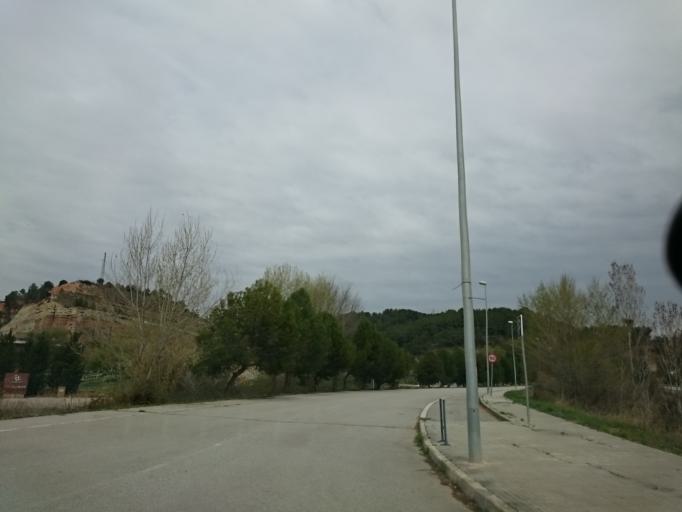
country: ES
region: Catalonia
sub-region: Provincia de Barcelona
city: Subirats
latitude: 41.4279
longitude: 1.8164
